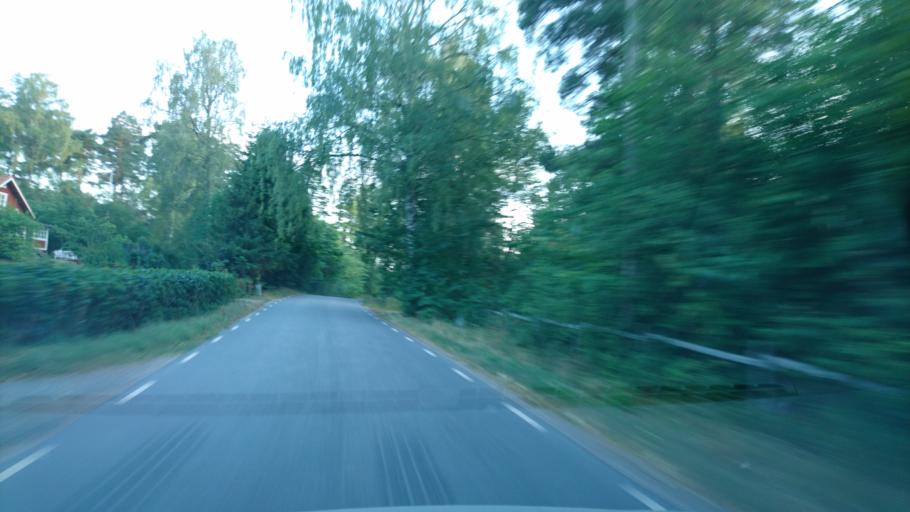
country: SE
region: Uppsala
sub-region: Uppsala Kommun
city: Saevja
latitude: 59.8098
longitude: 17.6779
